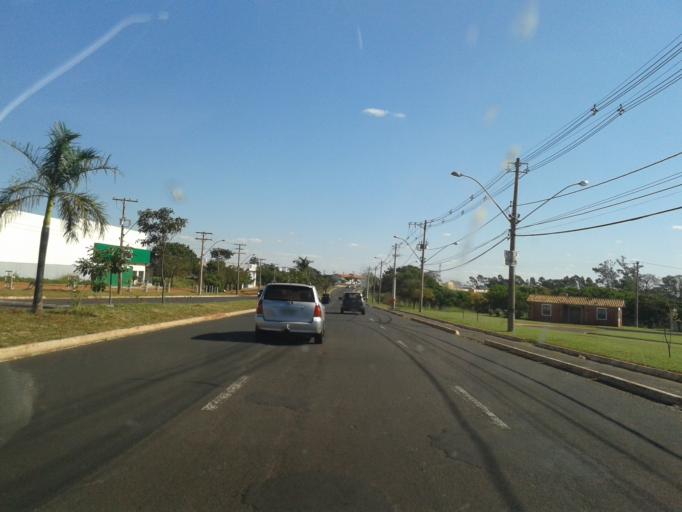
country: BR
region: Minas Gerais
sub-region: Uberaba
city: Uberaba
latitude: -19.7471
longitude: -47.9679
